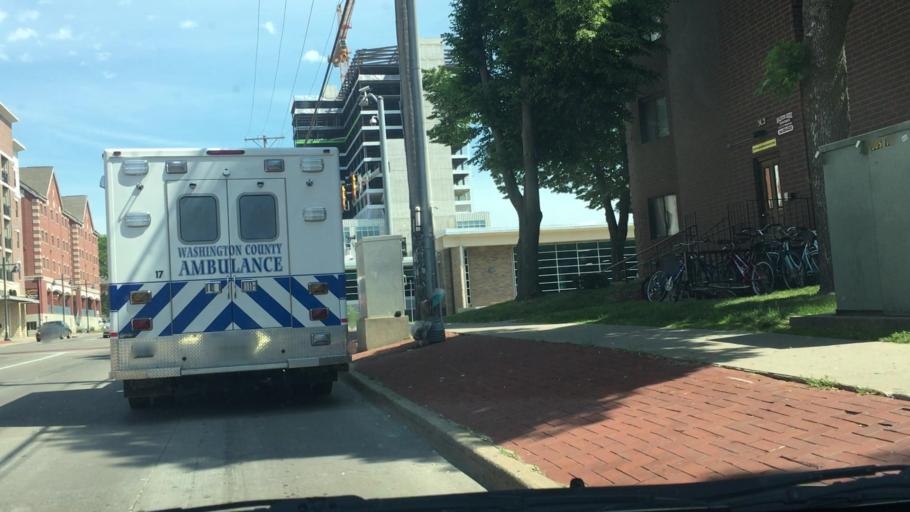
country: US
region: Iowa
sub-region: Johnson County
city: Iowa City
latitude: 41.6574
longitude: -91.5301
